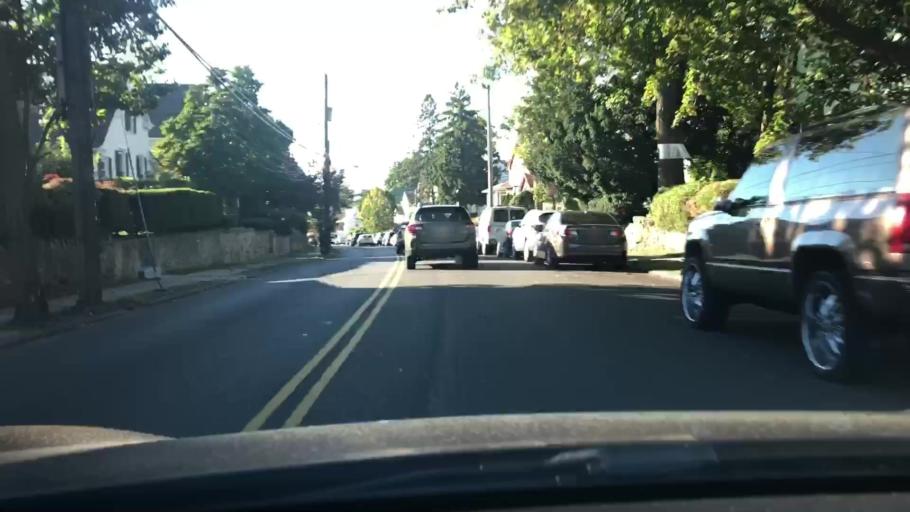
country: US
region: New York
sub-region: Westchester County
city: Pelham
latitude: 40.9042
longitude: -73.8212
